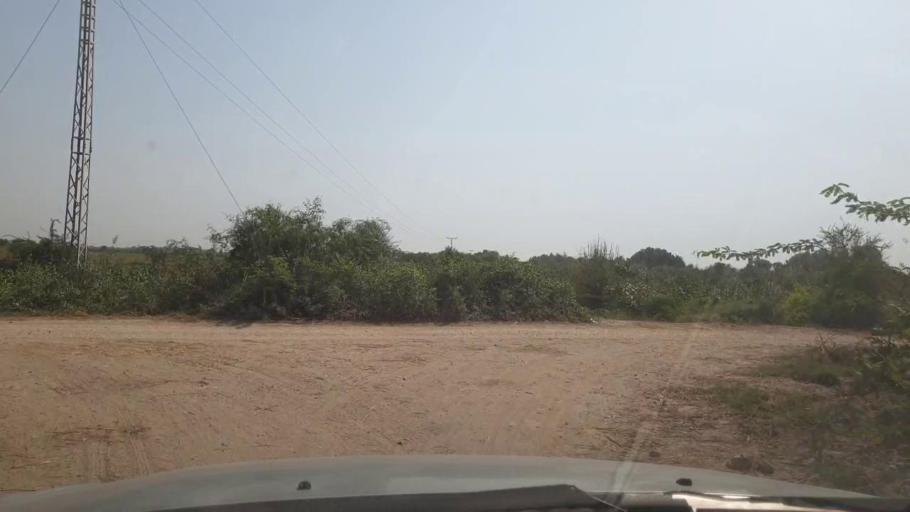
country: PK
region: Sindh
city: Bulri
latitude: 24.8642
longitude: 68.3110
